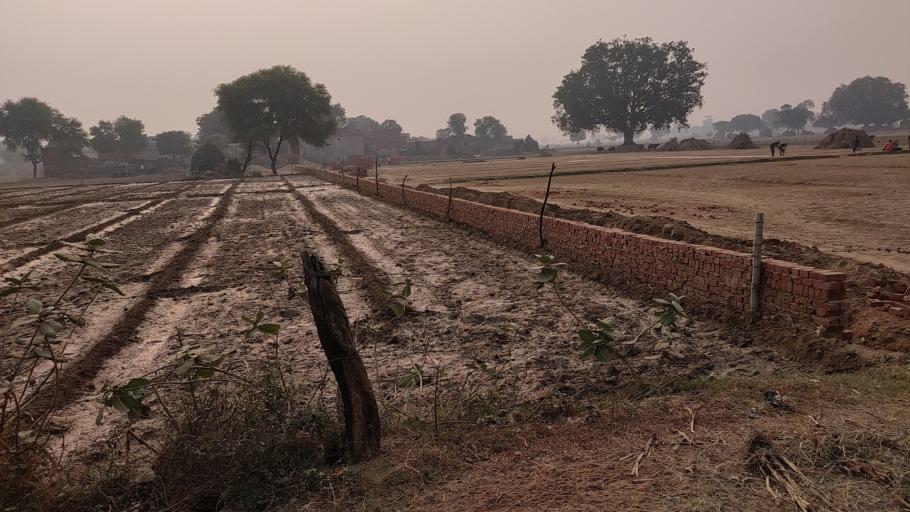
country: IN
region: Uttar Pradesh
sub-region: Mathura
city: Vrindavan
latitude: 27.5551
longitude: 77.7158
